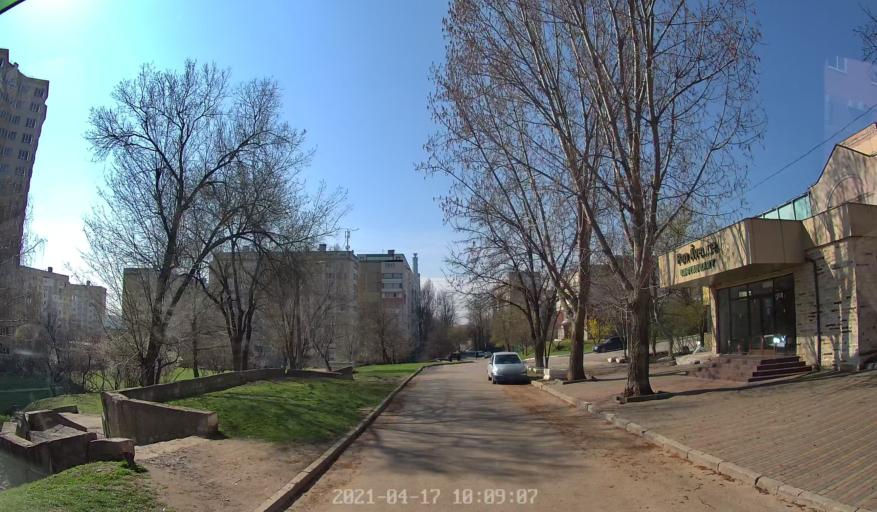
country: MD
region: Chisinau
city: Chisinau
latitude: 47.0404
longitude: 28.8928
